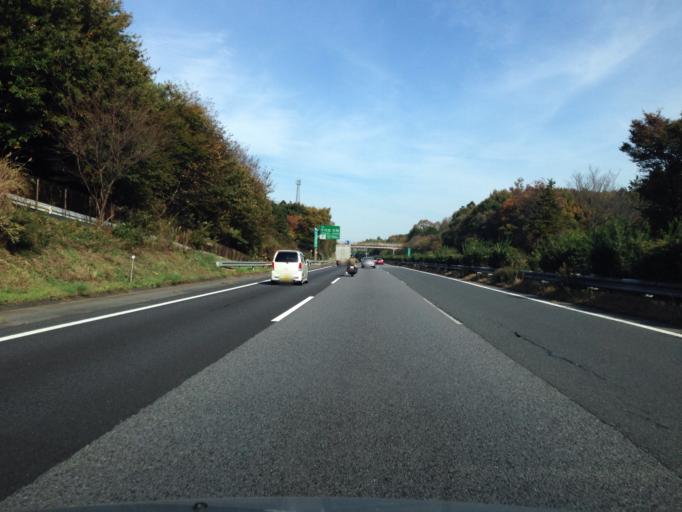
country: JP
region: Ibaraki
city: Ishioka
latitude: 36.1664
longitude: 140.2371
